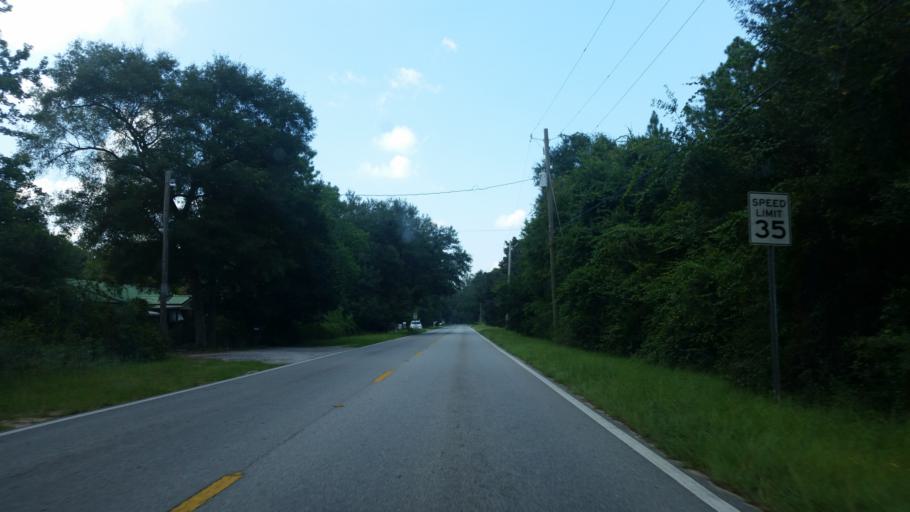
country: US
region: Florida
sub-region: Santa Rosa County
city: Bagdad
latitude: 30.5877
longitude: -87.0310
